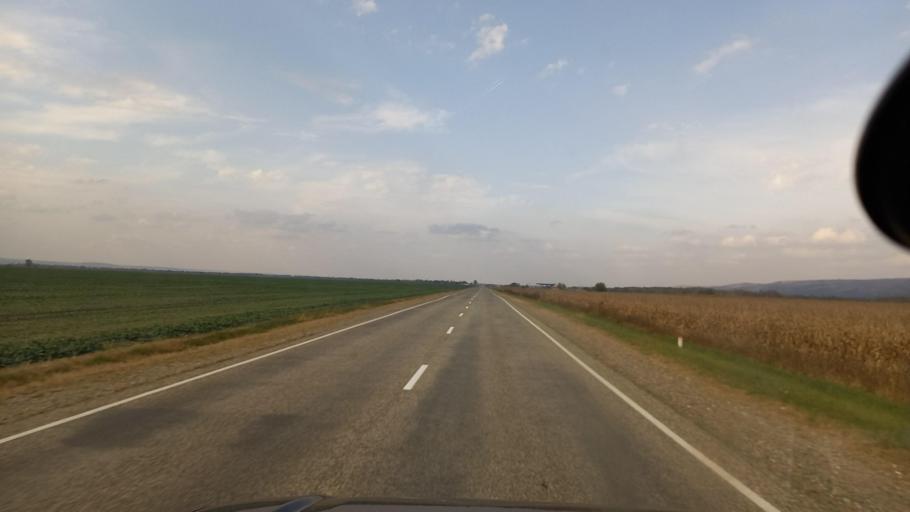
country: RU
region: Krasnodarskiy
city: Perepravnaya
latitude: 44.3280
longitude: 40.8496
